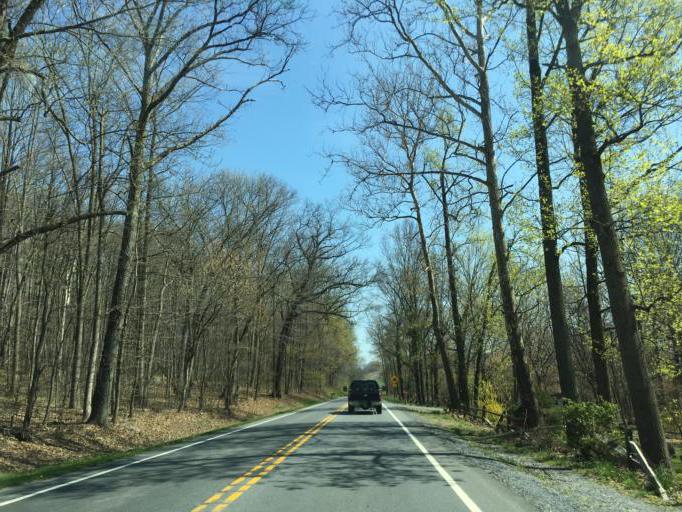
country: US
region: Maryland
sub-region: Frederick County
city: Woodsboro
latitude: 39.5034
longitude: -77.2705
